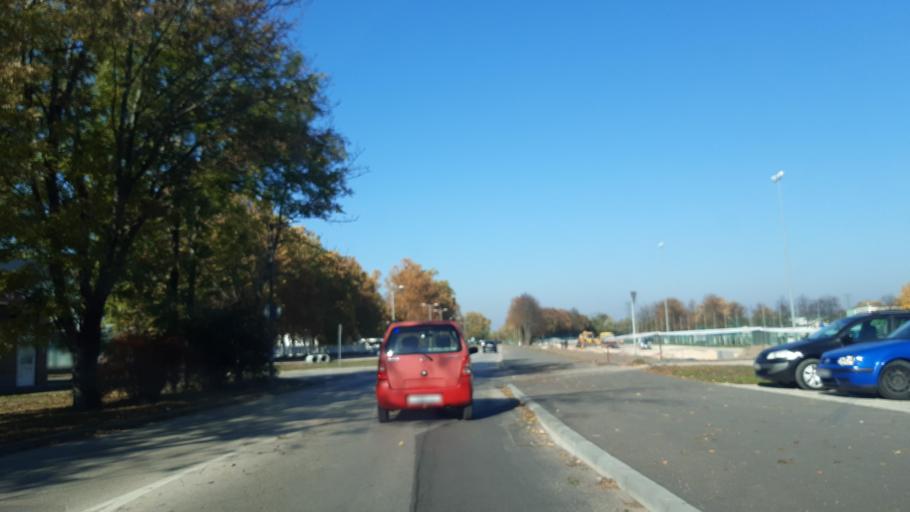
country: HU
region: Veszprem
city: Ajka
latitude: 47.1090
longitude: 17.5516
